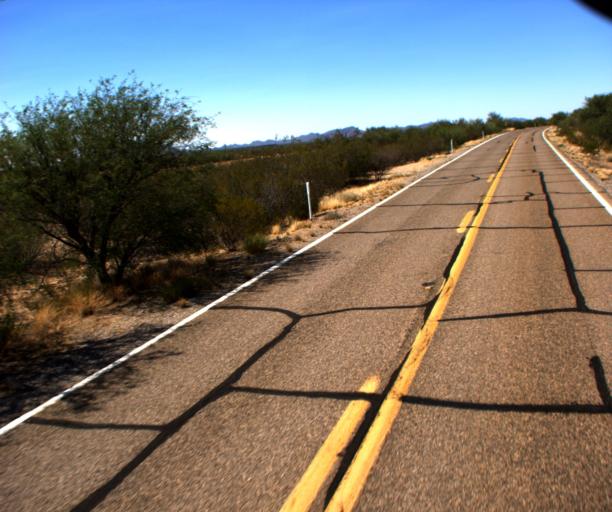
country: US
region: Arizona
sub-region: Pima County
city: Three Points
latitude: 31.9563
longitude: -111.3881
